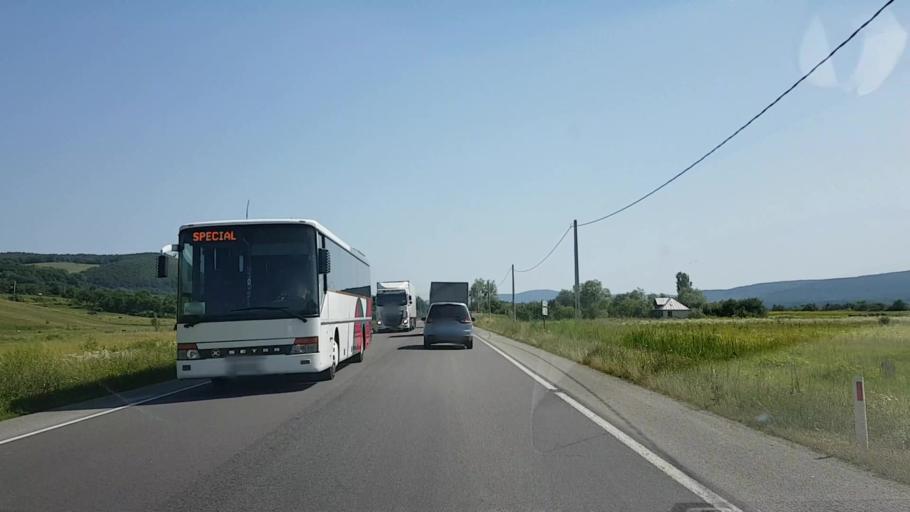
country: RO
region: Bistrita-Nasaud
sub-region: Comuna Sieu-Odorhei
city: Sieu-Odorhei
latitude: 47.1568
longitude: 24.3063
